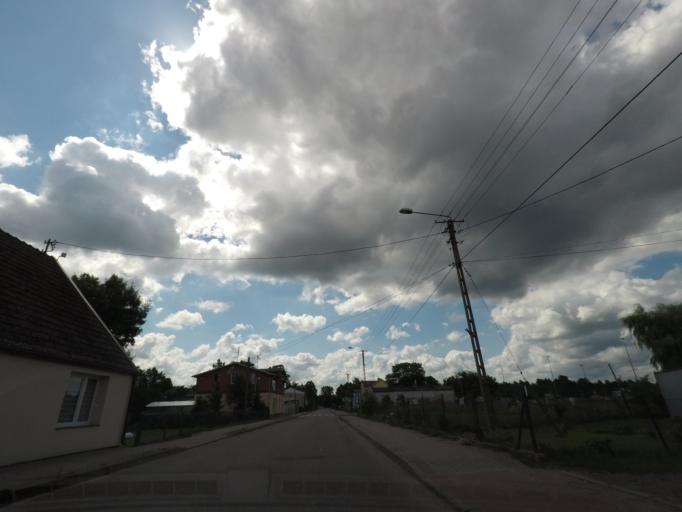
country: PL
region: Pomeranian Voivodeship
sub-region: Powiat wejherowski
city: Leczyce
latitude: 54.5927
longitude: 17.8610
